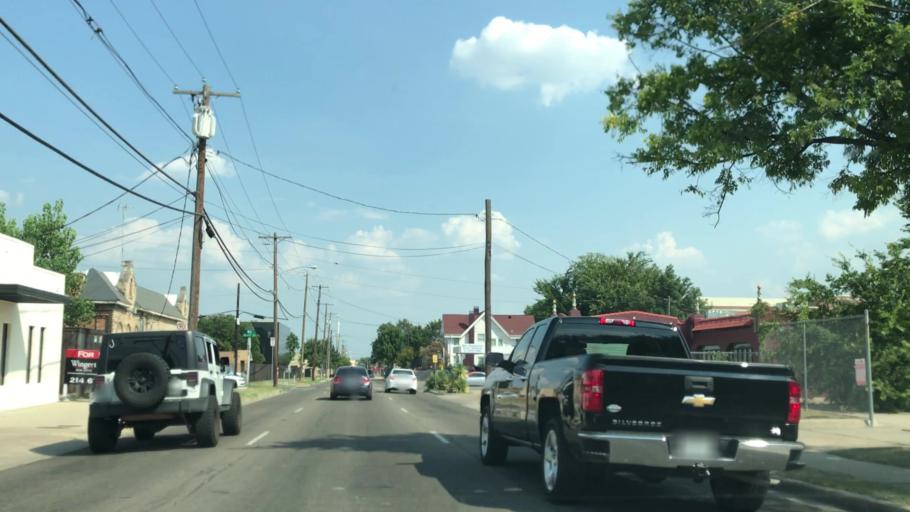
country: US
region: Texas
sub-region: Dallas County
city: Dallas
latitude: 32.7926
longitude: -96.7754
